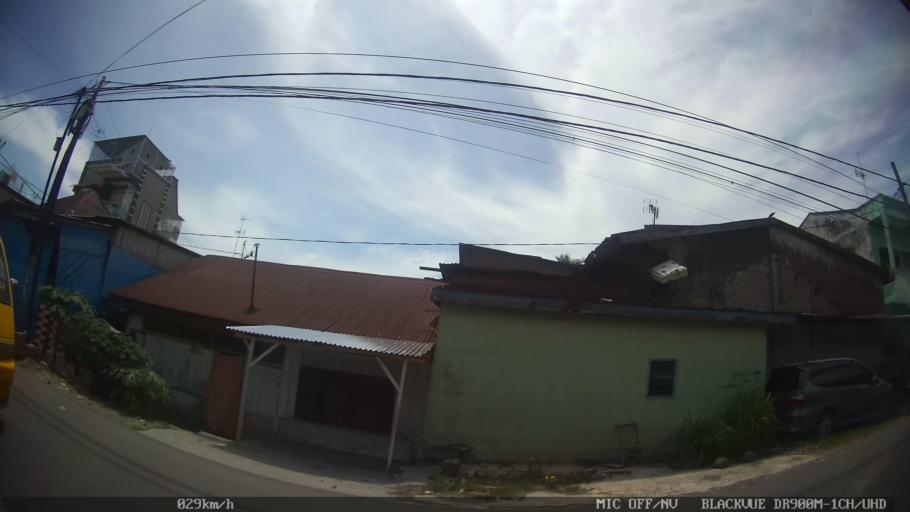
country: ID
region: North Sumatra
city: Binjai
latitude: 3.6057
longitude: 98.4902
